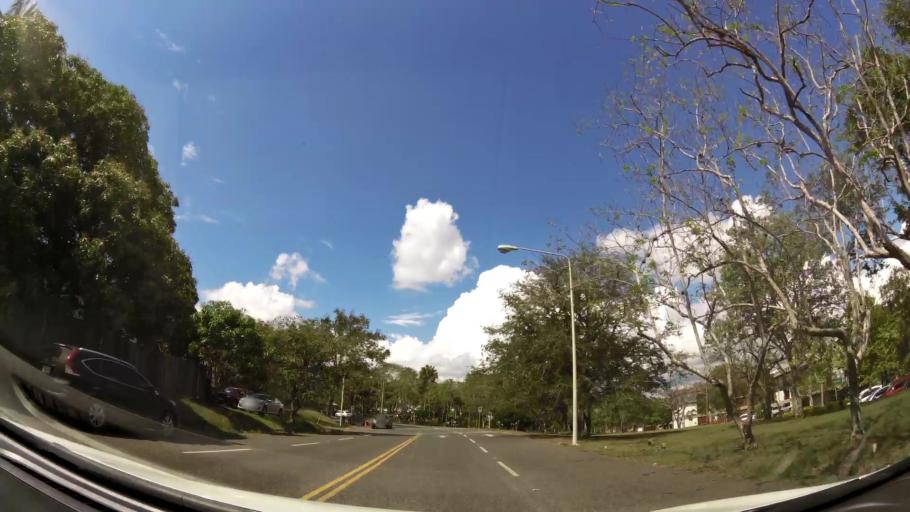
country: DO
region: Santiago
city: Santiago de los Caballeros
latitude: 19.4405
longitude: -70.6840
